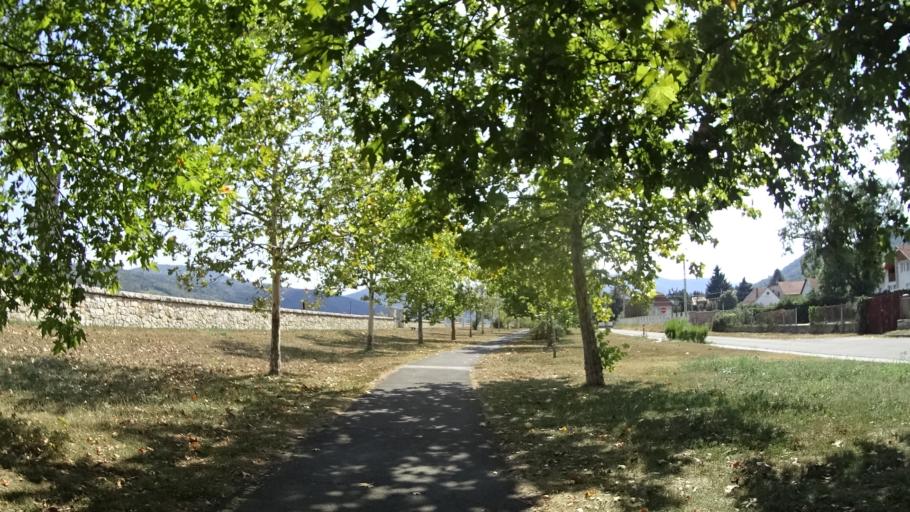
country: HU
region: Pest
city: Nagymaros
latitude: 47.7853
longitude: 18.9591
